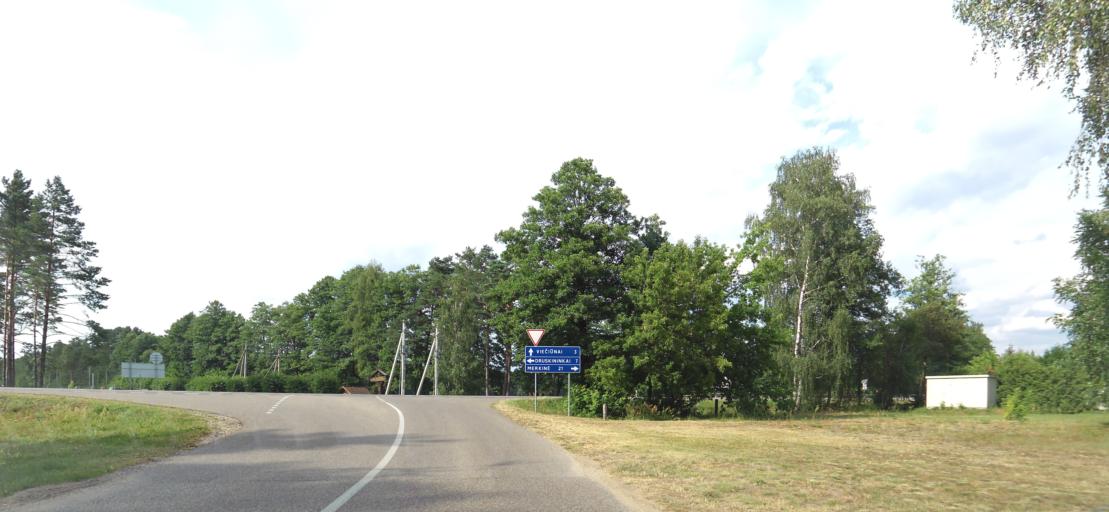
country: LT
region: Alytaus apskritis
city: Druskininkai
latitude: 54.0328
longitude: 24.0750
